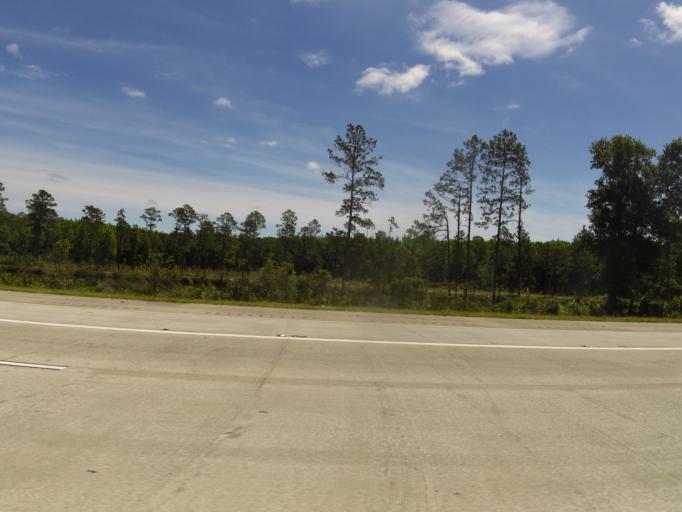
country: US
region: Georgia
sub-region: McIntosh County
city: Darien
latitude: 31.2984
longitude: -81.4823
